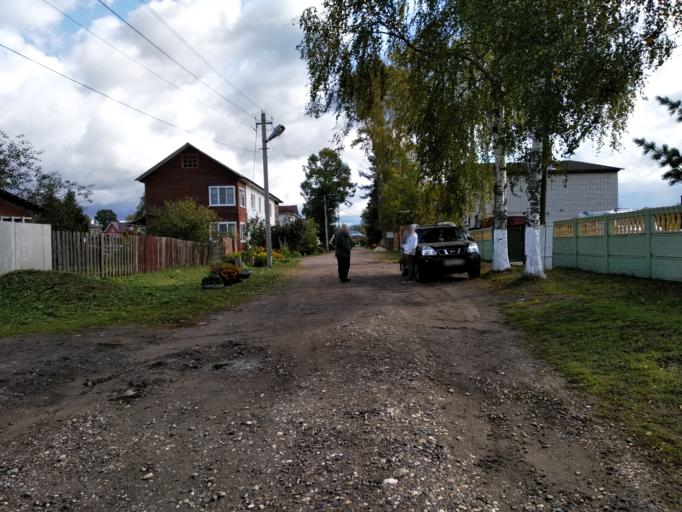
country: RU
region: Tverskaya
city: Kashin
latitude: 57.3618
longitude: 37.6171
